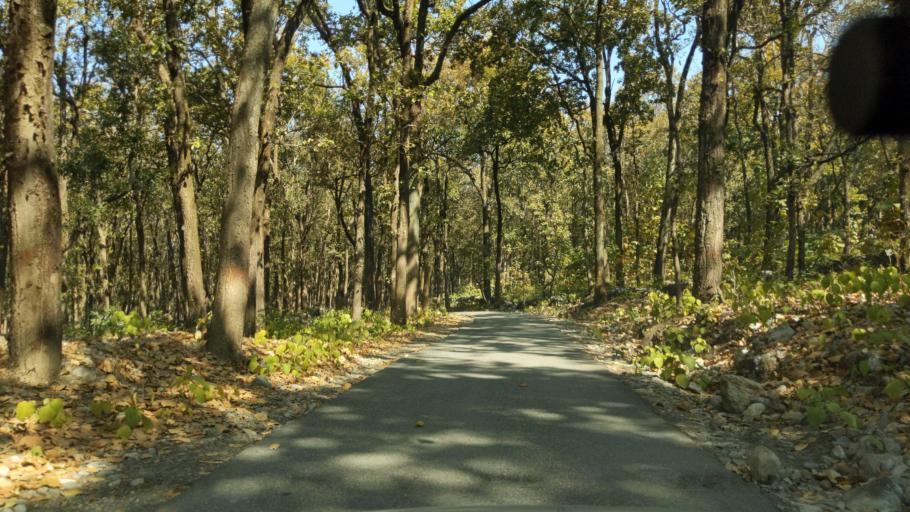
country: IN
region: Uttarakhand
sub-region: Naini Tal
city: Ramnagar
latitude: 29.4663
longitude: 79.2328
